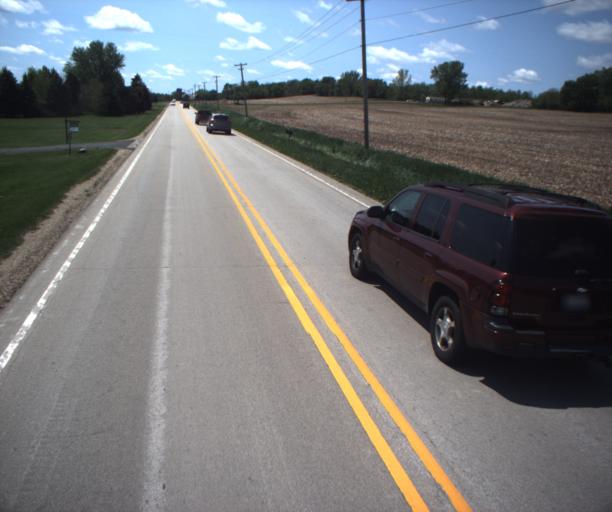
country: US
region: Illinois
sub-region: Kane County
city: North Aurora
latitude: 41.8518
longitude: -88.3979
